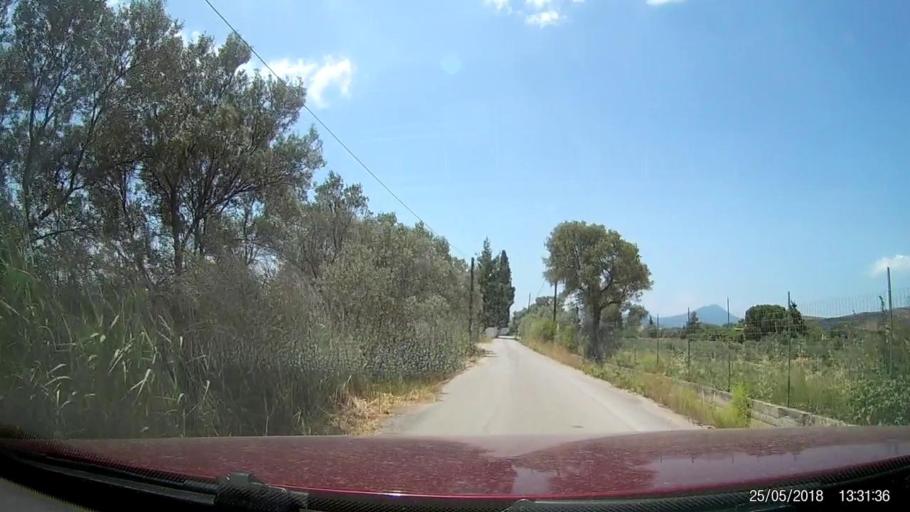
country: GR
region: Central Greece
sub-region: Nomos Evvoias
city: Mytikas
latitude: 38.4371
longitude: 23.6549
